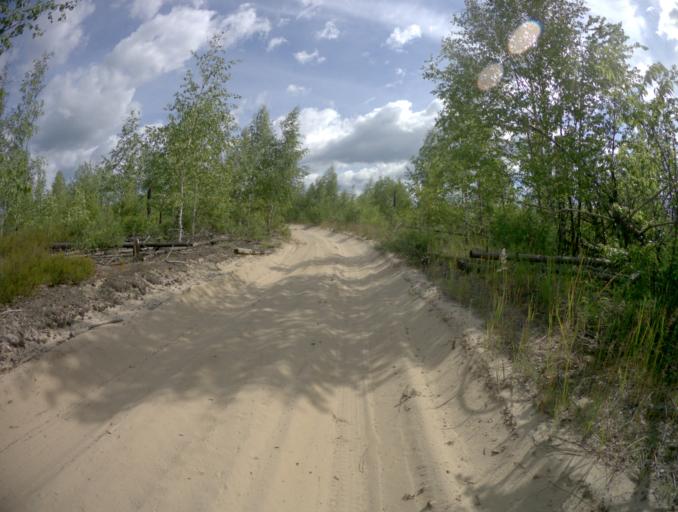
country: RU
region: Ivanovo
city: Talitsy
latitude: 56.5347
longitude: 42.4403
